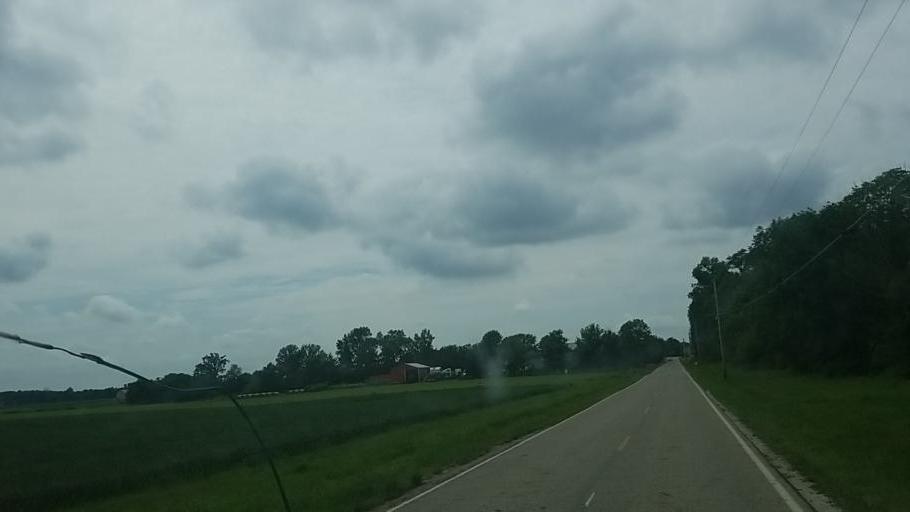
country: US
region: Ohio
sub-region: Fairfield County
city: Lithopolis
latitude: 39.7534
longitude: -82.8718
